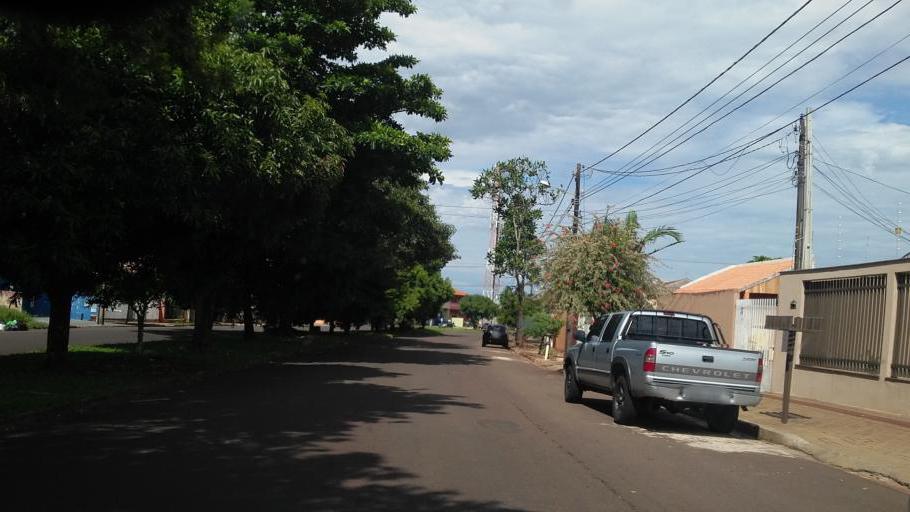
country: BR
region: Parana
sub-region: Londrina
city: Londrina
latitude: -23.2835
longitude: -51.1997
